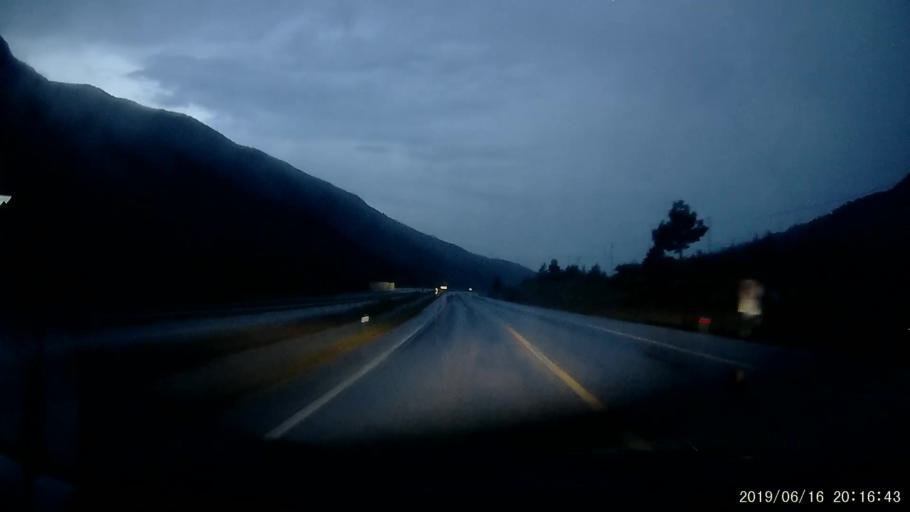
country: TR
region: Tokat
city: Resadiye
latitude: 40.3606
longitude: 37.4360
